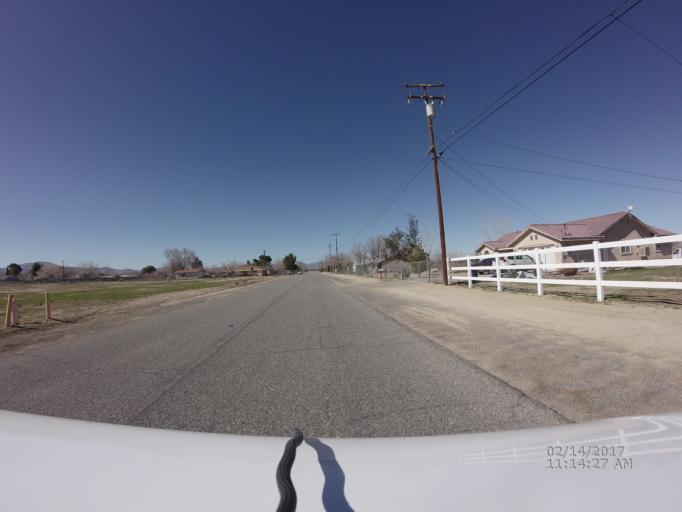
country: US
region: California
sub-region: Los Angeles County
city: Littlerock
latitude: 34.5615
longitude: -117.9640
